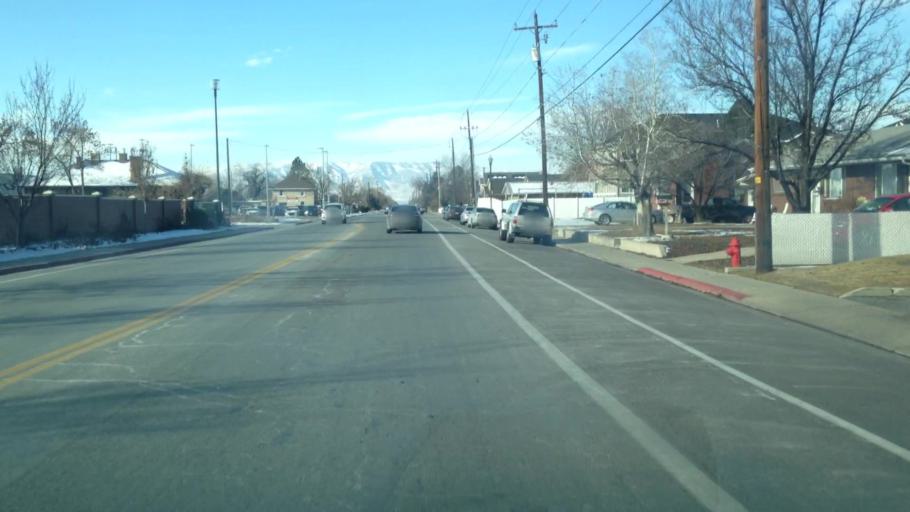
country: US
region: Utah
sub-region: Utah County
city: Orem
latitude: 40.2752
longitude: -111.6890
